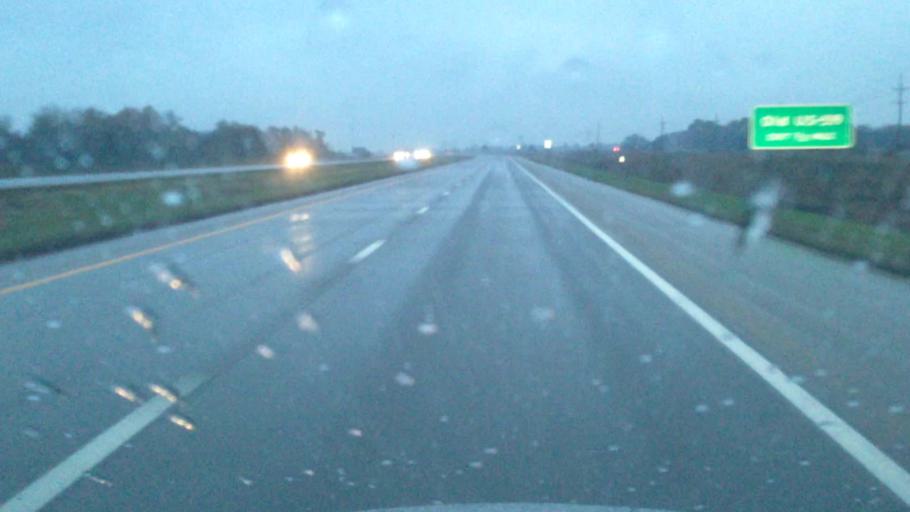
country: US
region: Kansas
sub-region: Franklin County
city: Ottawa
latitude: 38.7009
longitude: -95.2685
